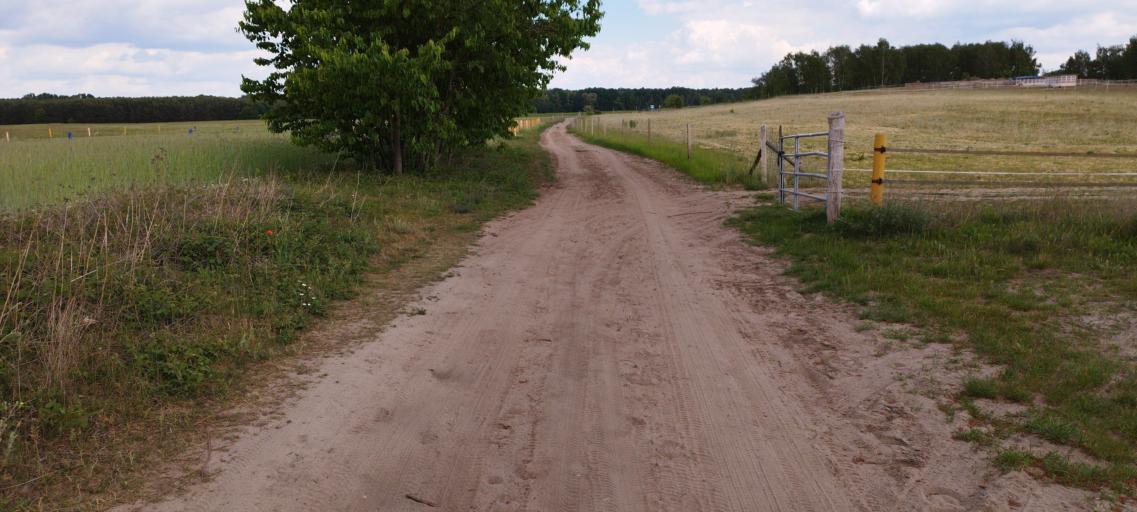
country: DE
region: Brandenburg
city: Wandlitz
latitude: 52.7270
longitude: 13.4208
